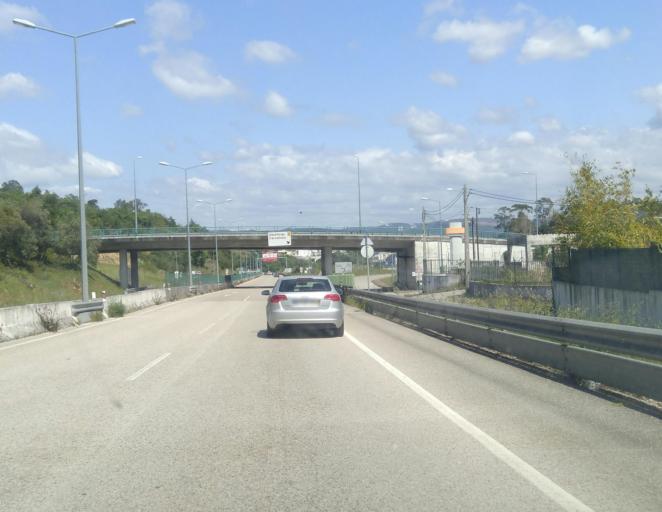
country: PT
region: Coimbra
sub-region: Coimbra
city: Coimbra
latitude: 40.1789
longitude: -8.4464
